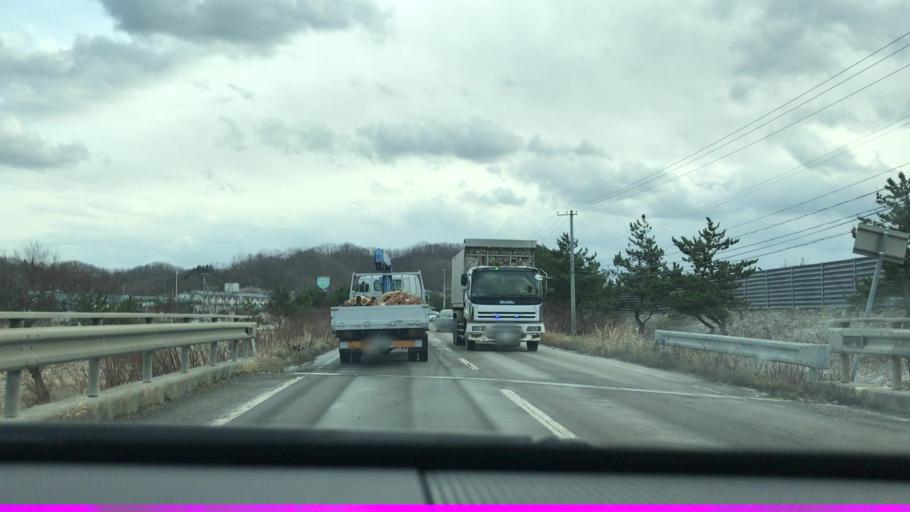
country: JP
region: Hokkaido
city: Shizunai-furukawacho
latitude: 42.3088
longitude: 142.4353
